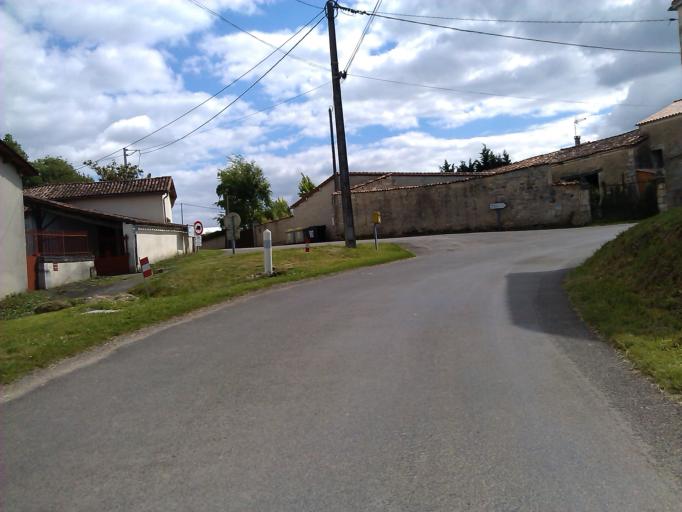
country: FR
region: Poitou-Charentes
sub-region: Departement de la Charente
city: Mansle
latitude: 45.9044
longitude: 0.2176
